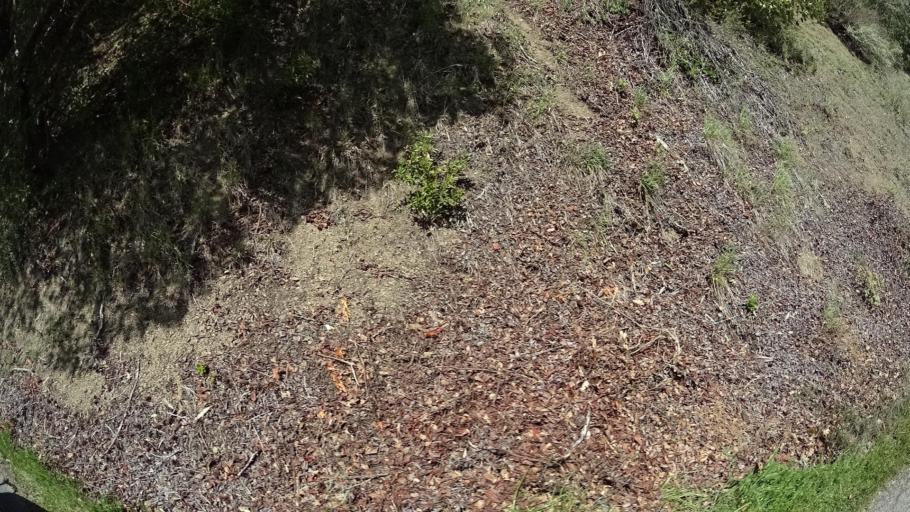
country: US
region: California
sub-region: Humboldt County
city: Redway
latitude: 40.3100
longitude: -123.6567
